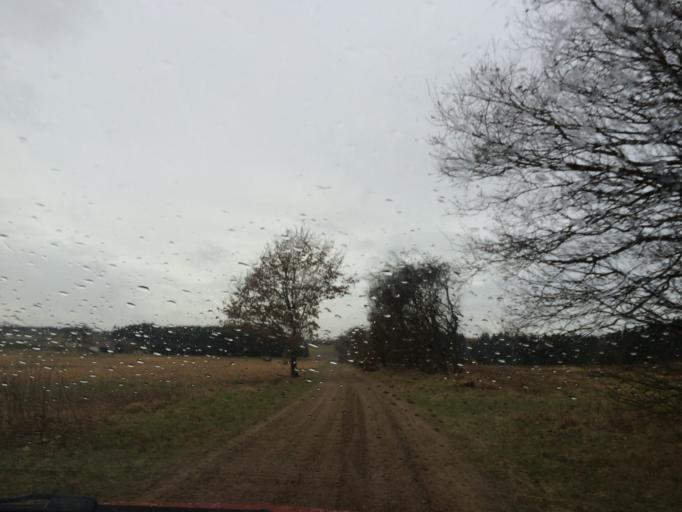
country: DK
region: Central Jutland
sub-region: Silkeborg Kommune
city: Virklund
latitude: 56.0235
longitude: 9.4731
